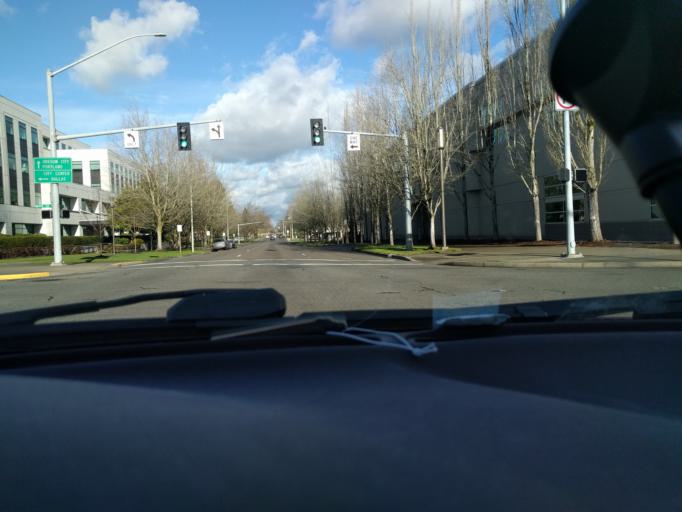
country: US
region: Oregon
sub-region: Marion County
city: Salem
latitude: 44.9418
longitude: -123.0269
